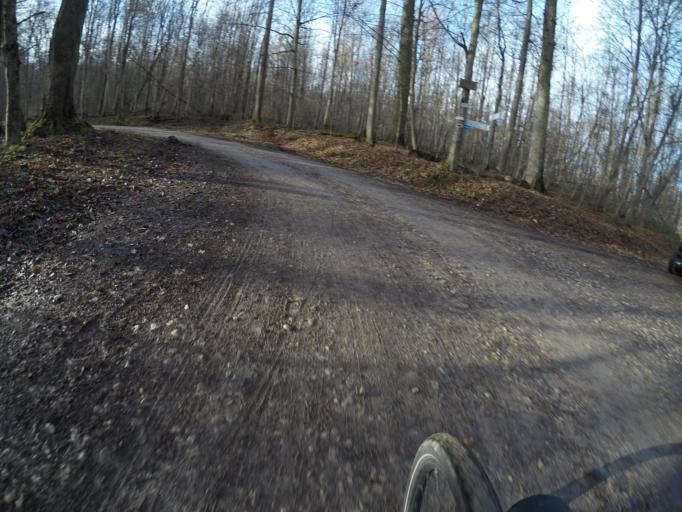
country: DE
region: Baden-Wuerttemberg
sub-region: Regierungsbezirk Stuttgart
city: Oberboihingen
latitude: 48.6339
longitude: 9.4010
